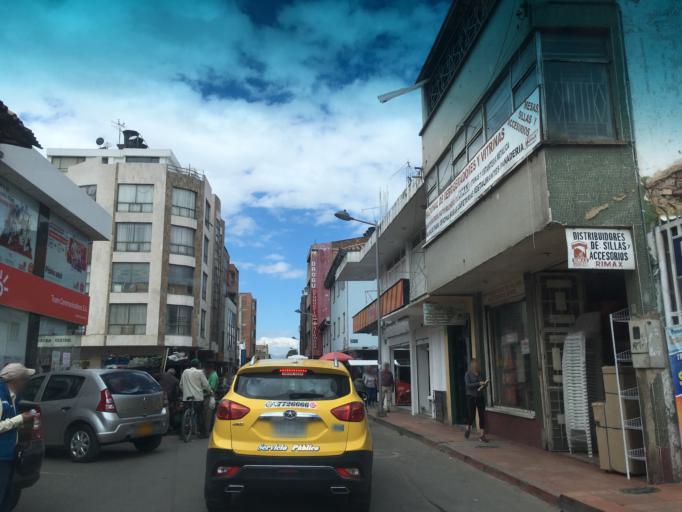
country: CO
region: Boyaca
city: Sogamoso
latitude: 5.7135
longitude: -72.9285
